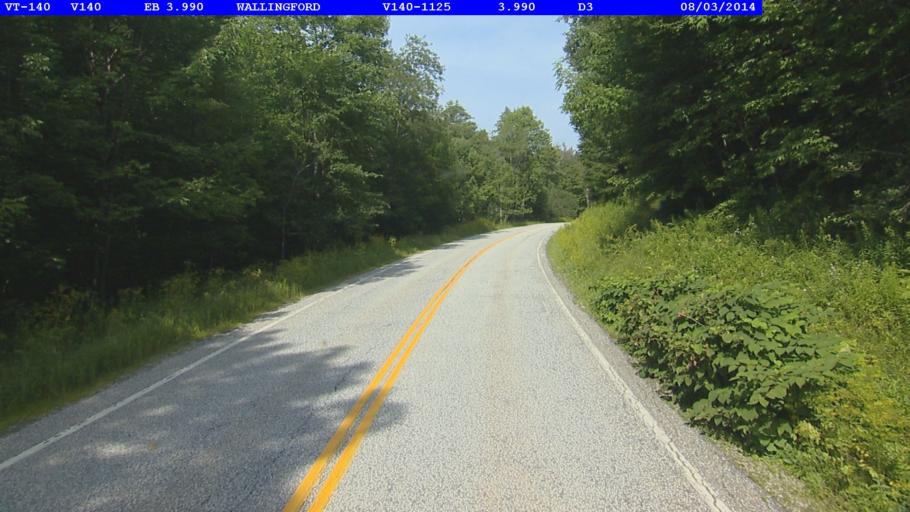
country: US
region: Vermont
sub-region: Rutland County
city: Rutland
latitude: 43.4593
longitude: -72.9111
